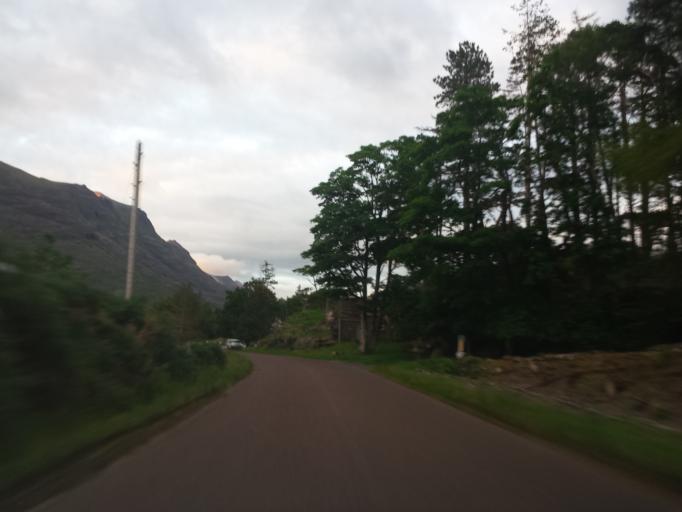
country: GB
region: Scotland
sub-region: Highland
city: Ullapool
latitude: 57.5308
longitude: -5.5201
